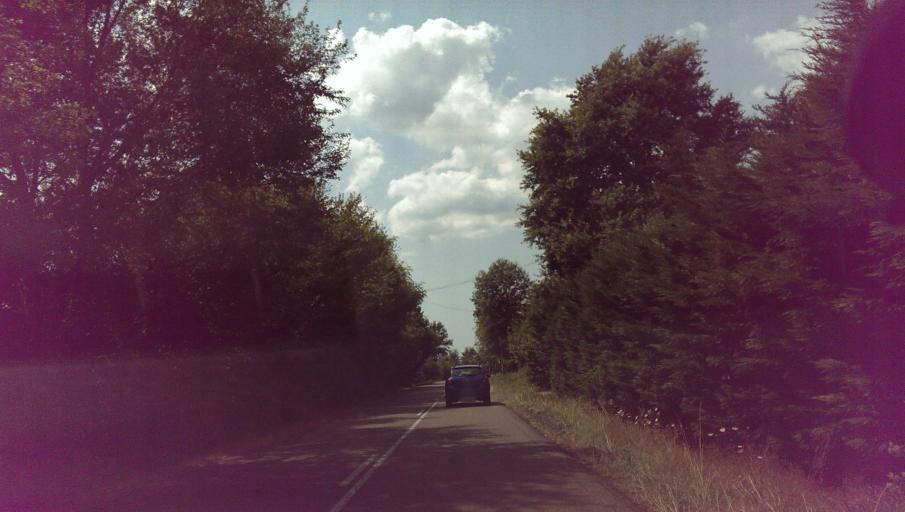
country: FR
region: Aquitaine
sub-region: Departement des Landes
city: Sabres
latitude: 44.1229
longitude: -0.6690
